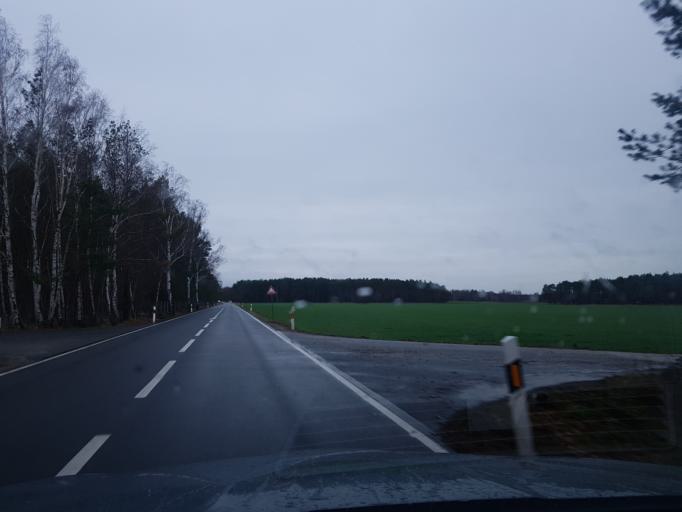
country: DE
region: Brandenburg
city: Finsterwalde
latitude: 51.6583
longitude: 13.6906
